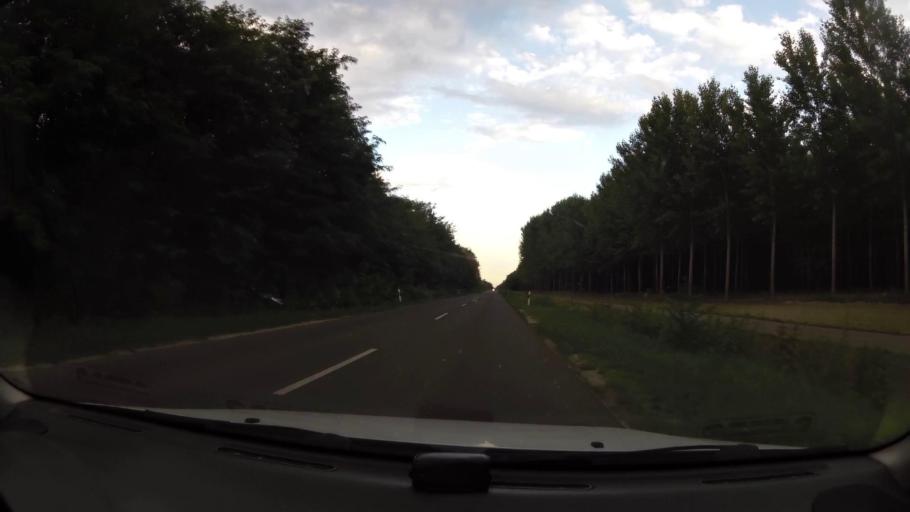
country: HU
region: Pest
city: Ujszilvas
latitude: 47.2899
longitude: 19.9063
